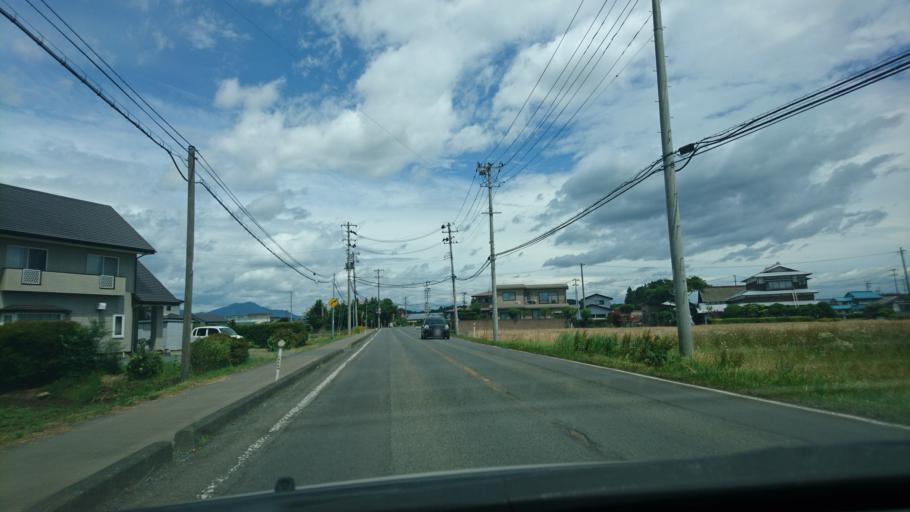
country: JP
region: Iwate
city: Morioka-shi
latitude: 39.5449
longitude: 141.1796
